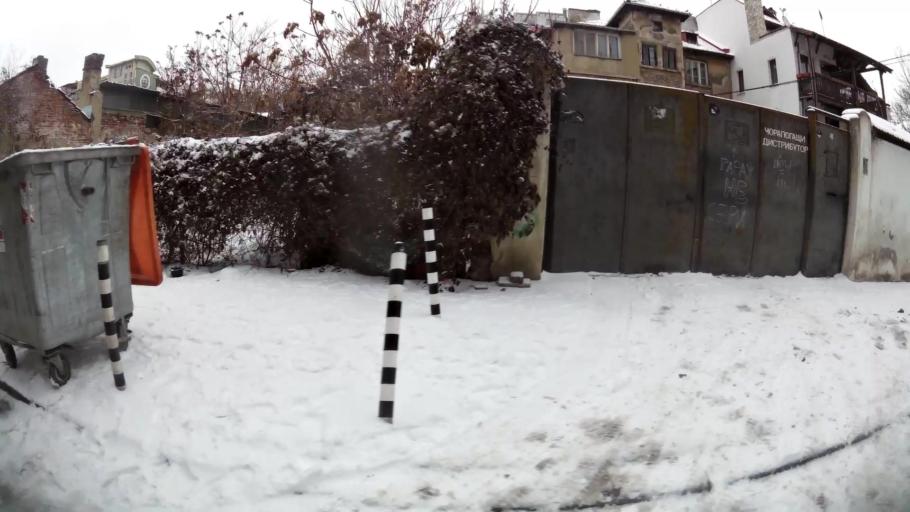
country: BG
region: Sofia-Capital
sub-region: Stolichna Obshtina
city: Sofia
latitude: 42.7059
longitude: 23.3312
